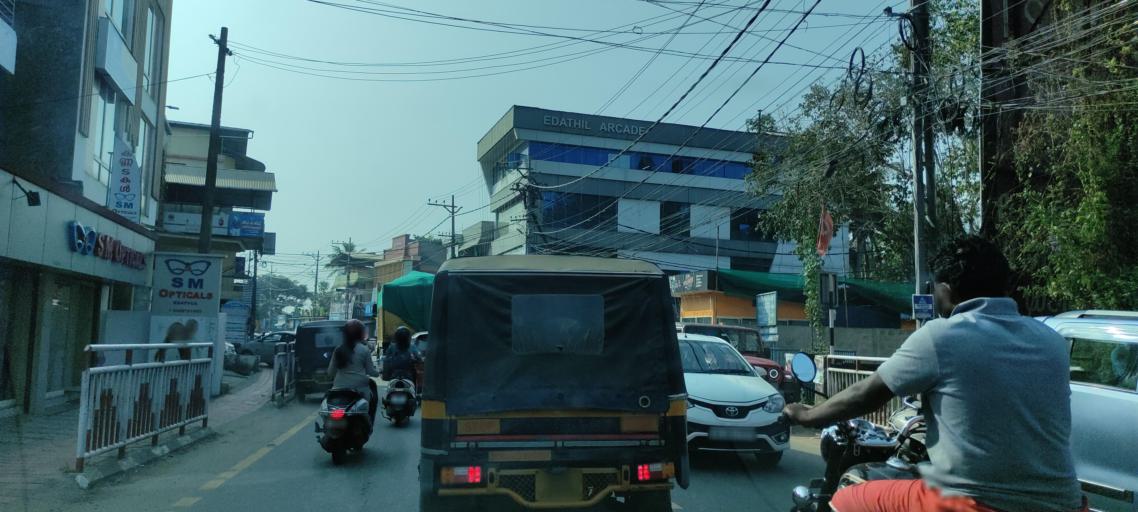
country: IN
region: Kerala
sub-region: Kottayam
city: Changanacheri
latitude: 9.3671
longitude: 76.4793
